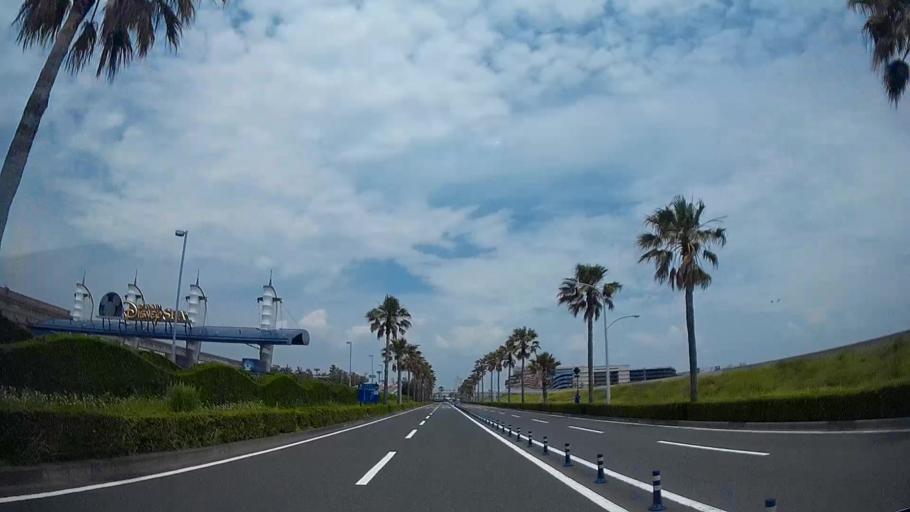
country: JP
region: Tokyo
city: Urayasu
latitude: 35.6237
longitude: 139.8896
